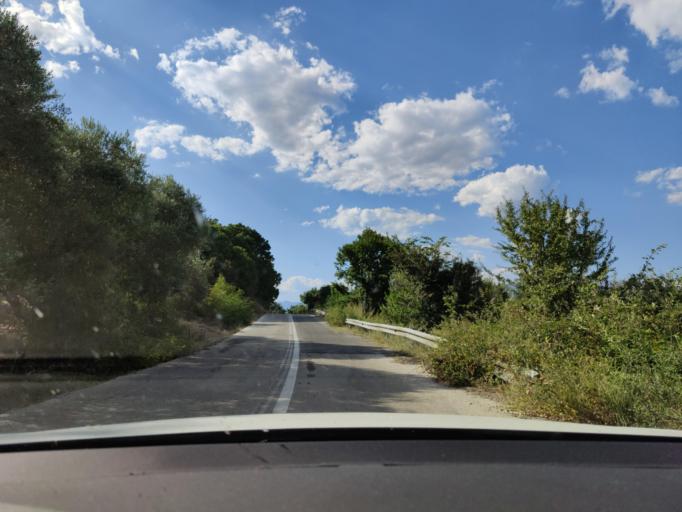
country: GR
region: Central Macedonia
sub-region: Nomos Serron
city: Chrysochorafa
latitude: 41.1680
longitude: 23.1791
